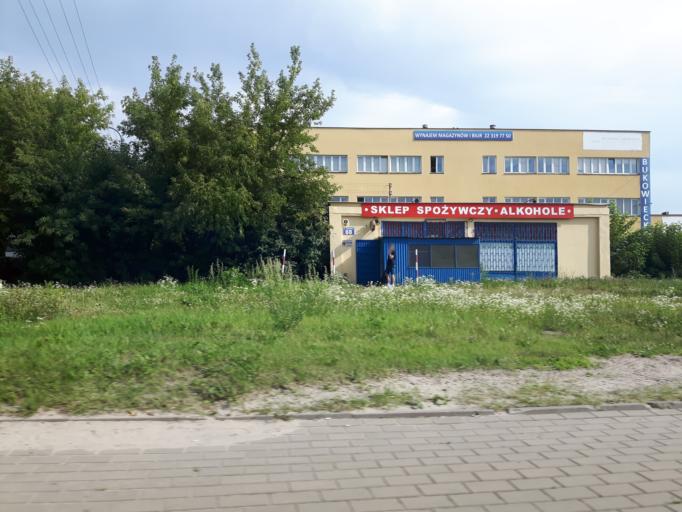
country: PL
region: Masovian Voivodeship
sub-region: Warszawa
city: Praga Poludnie
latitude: 52.2703
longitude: 21.0792
